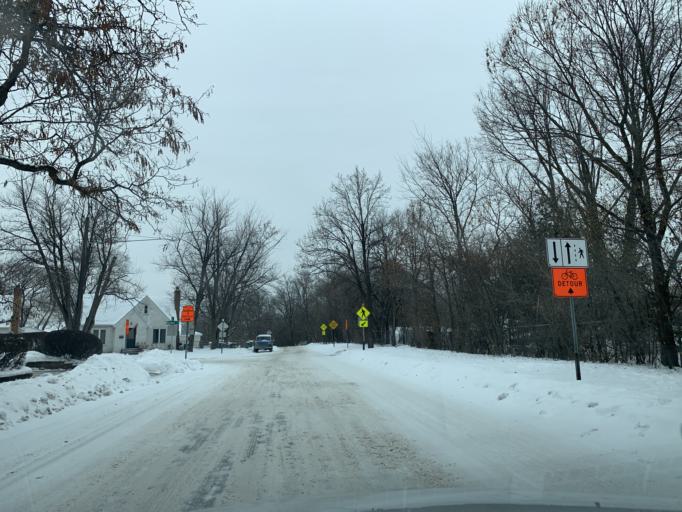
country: US
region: Minnesota
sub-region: Hennepin County
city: Saint Louis Park
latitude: 44.9432
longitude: -93.3291
